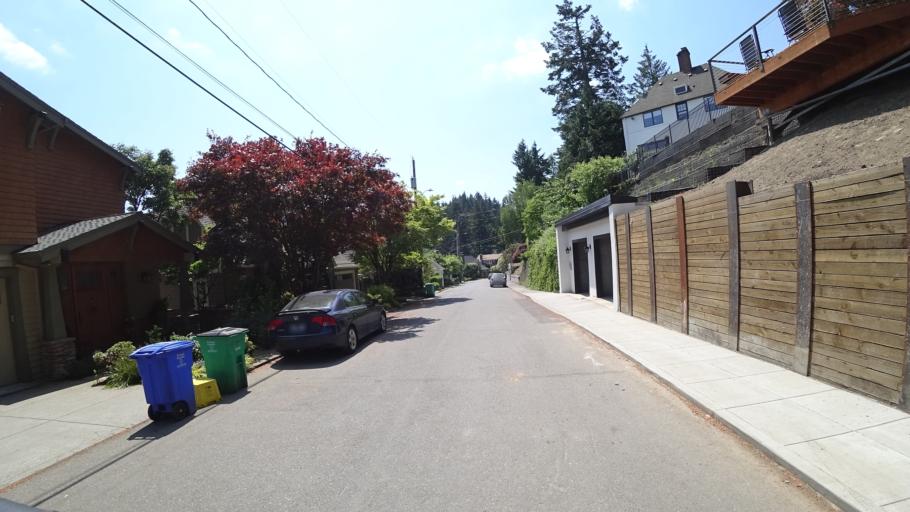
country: US
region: Oregon
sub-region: Multnomah County
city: Portland
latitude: 45.5219
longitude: -122.7084
